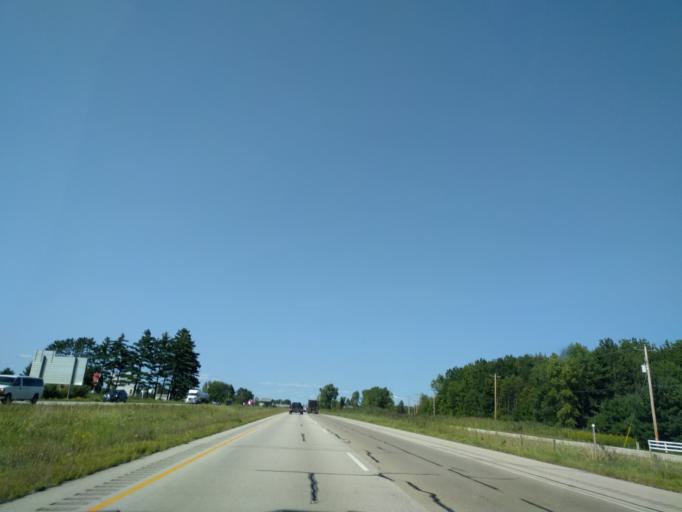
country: US
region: Wisconsin
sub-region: Brown County
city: Suamico
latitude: 44.6529
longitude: -88.0499
